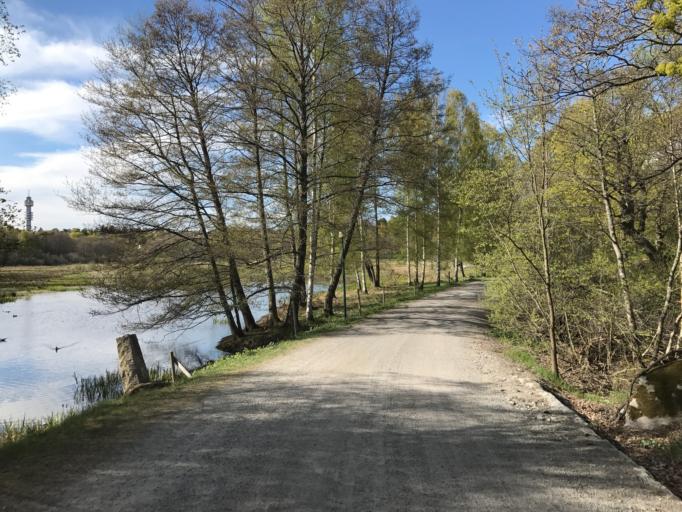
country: SE
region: Stockholm
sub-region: Nacka Kommun
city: Nacka
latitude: 59.3240
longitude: 18.1444
